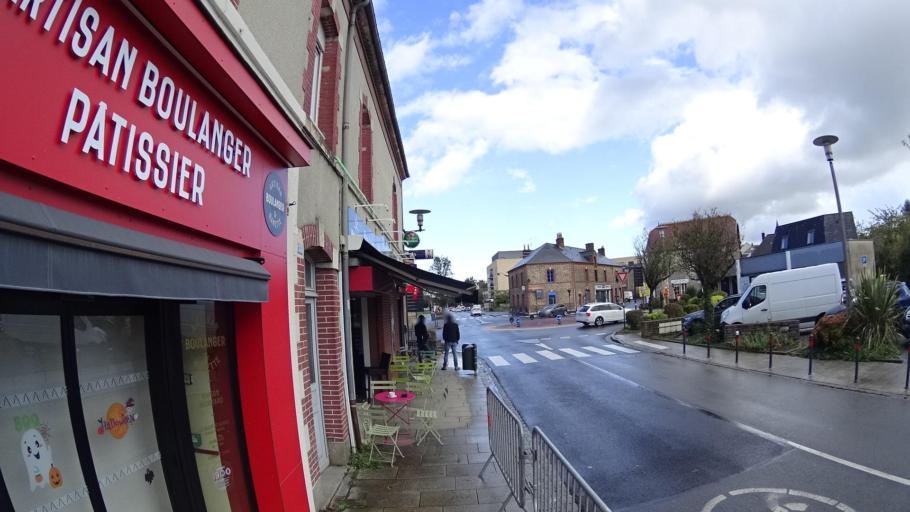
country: FR
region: Brittany
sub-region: Departement d'Ille-et-Vilaine
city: Chatillon-sur-Seiche
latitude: 48.0411
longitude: -1.6665
